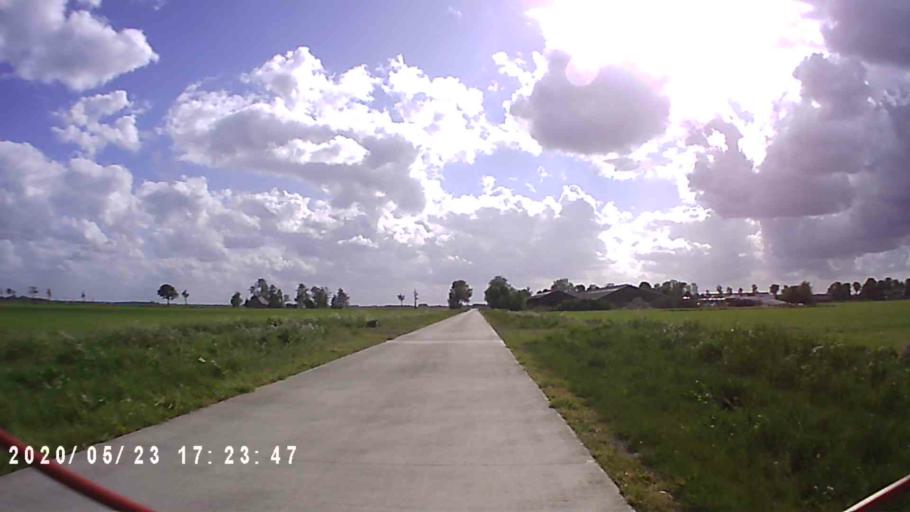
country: NL
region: Groningen
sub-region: Gemeente Slochteren
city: Slochteren
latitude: 53.2581
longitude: 6.7886
